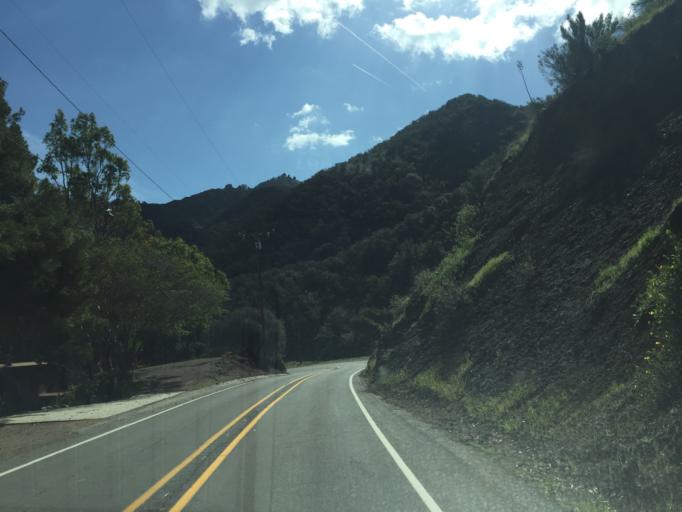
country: US
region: California
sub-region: Los Angeles County
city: Malibu Beach
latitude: 34.0727
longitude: -118.6856
